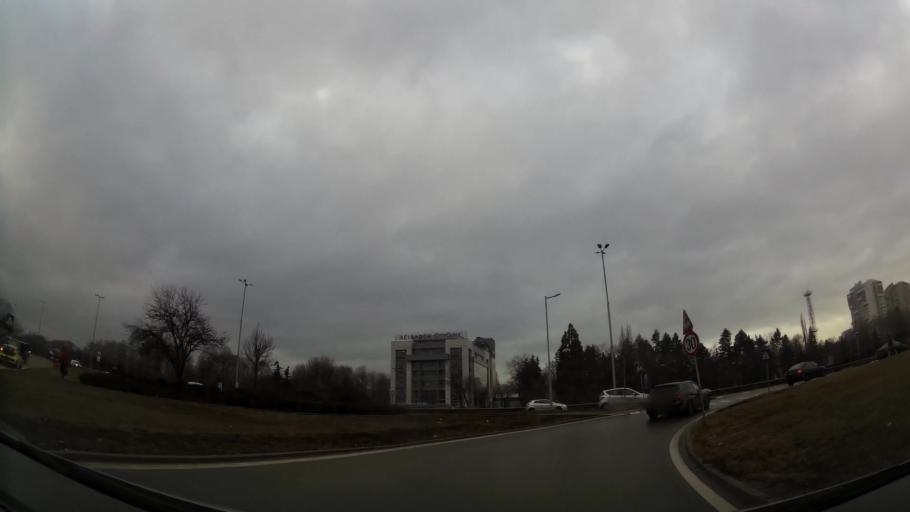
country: BG
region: Sofia-Capital
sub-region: Stolichna Obshtina
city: Sofia
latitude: 42.6564
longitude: 23.3864
